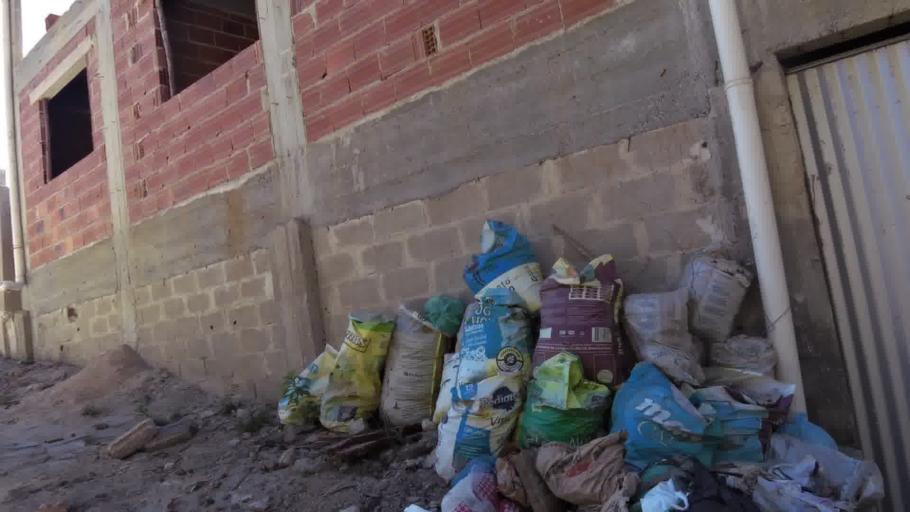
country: BR
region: Espirito Santo
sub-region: Vargem Alta
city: Vargem Alta
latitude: -20.6775
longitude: -41.0135
